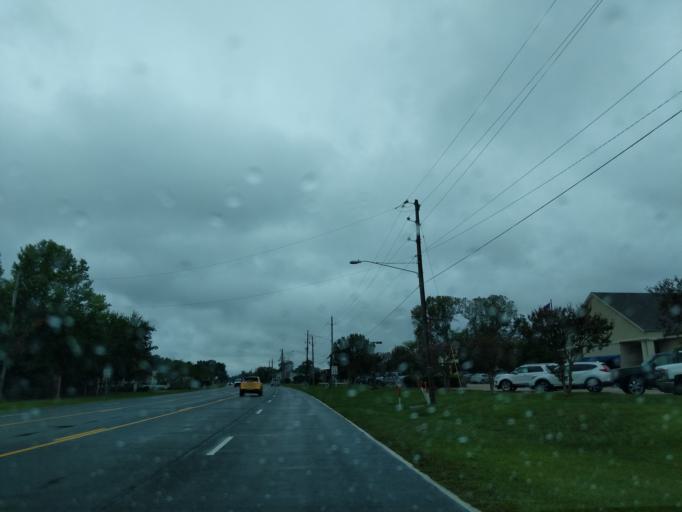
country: US
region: Louisiana
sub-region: Bossier Parish
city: Bossier City
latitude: 32.5120
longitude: -93.6833
